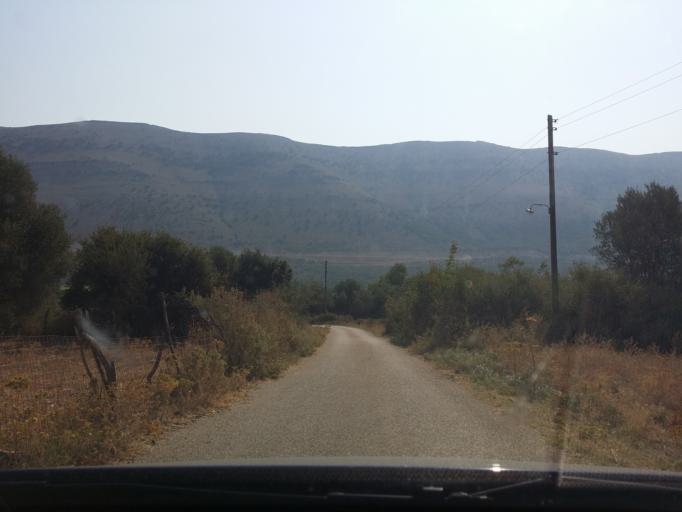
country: GR
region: West Greece
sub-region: Nomos Aitolias kai Akarnanias
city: Stanos
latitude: 38.8265
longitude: 21.1707
